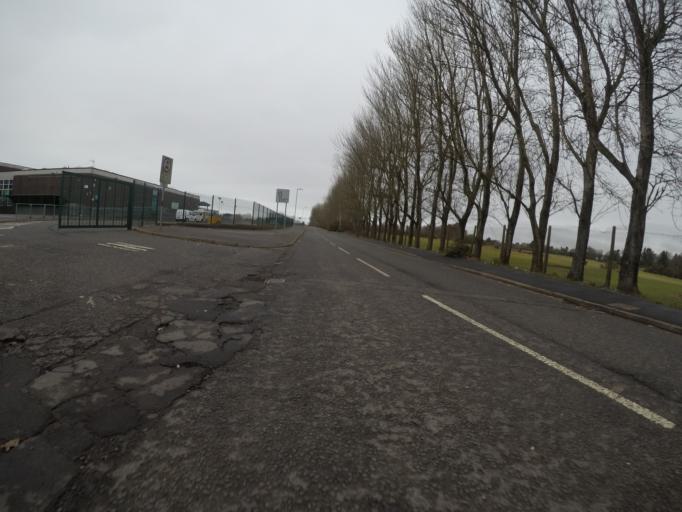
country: GB
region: Scotland
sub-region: North Ayrshire
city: Irvine
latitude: 55.6290
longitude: -4.6752
